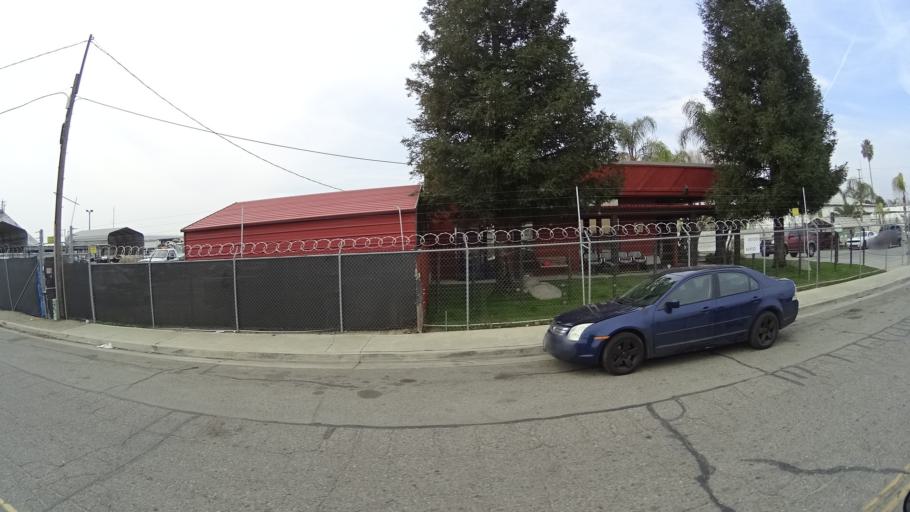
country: US
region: California
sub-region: Kern County
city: Bakersfield
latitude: 35.3718
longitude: -118.9764
